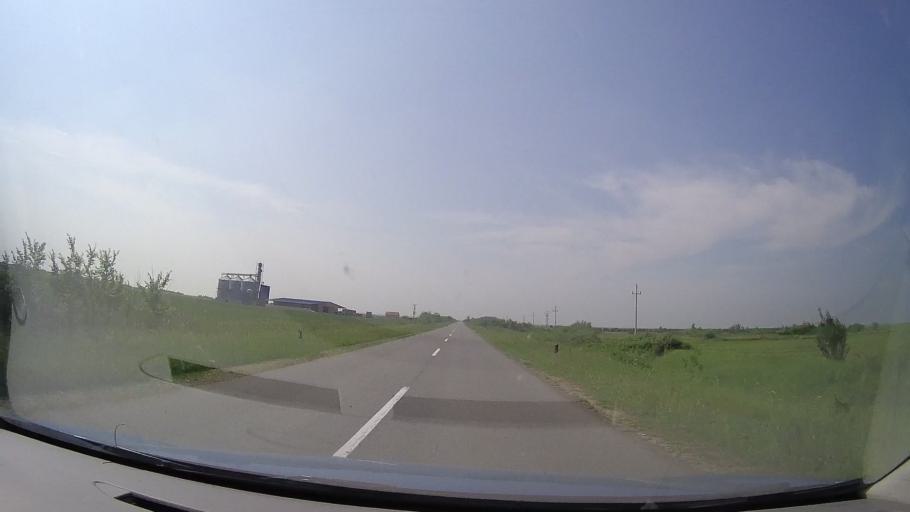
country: RS
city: Jarkovac
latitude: 45.2557
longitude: 20.7639
